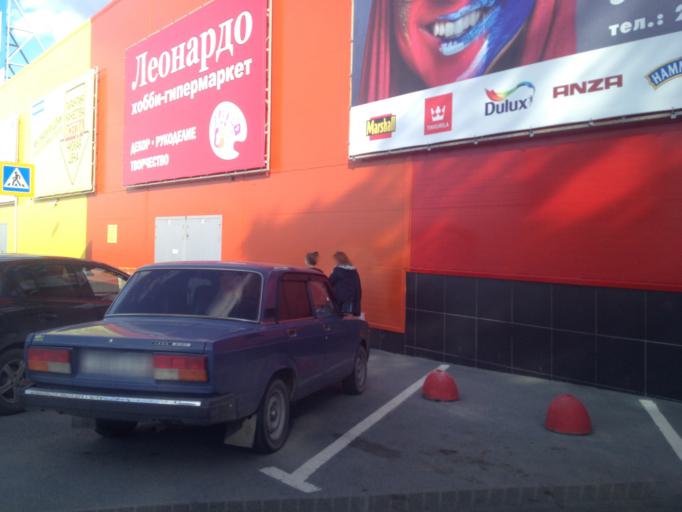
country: RU
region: Sverdlovsk
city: Shirokaya Rechka
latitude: 56.8167
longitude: 60.5344
